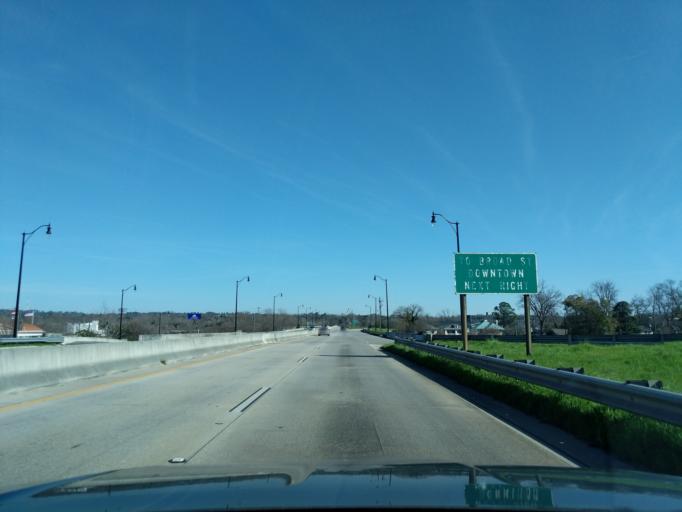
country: US
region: Georgia
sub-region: Richmond County
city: Augusta
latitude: 33.4708
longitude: -81.9578
